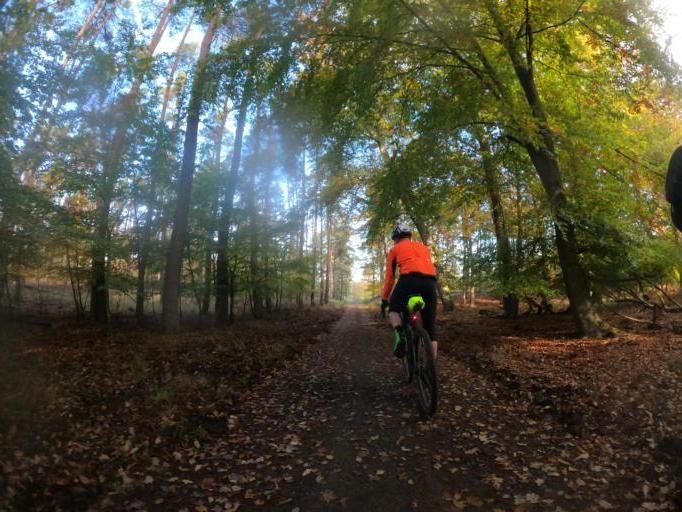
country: DE
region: Hesse
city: Raunheim
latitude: 49.9994
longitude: 8.4882
